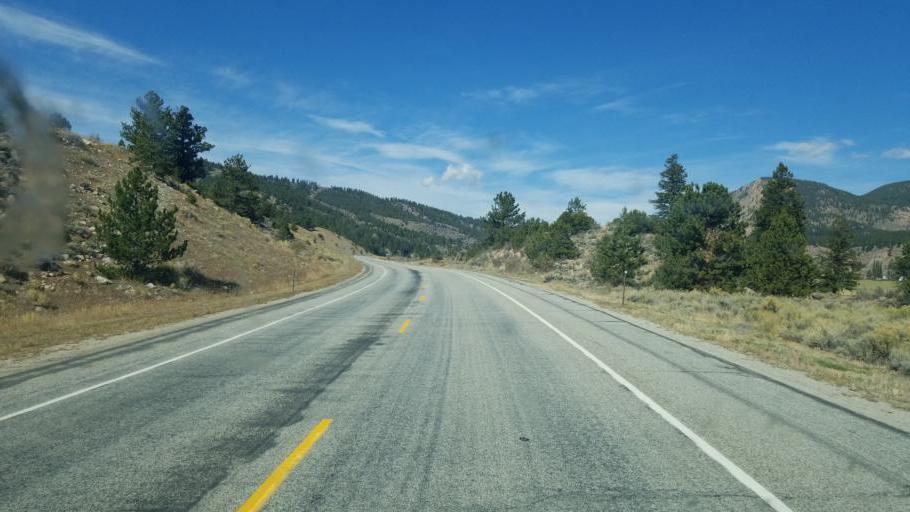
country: US
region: Colorado
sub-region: Chaffee County
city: Buena Vista
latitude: 38.9696
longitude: -106.2077
